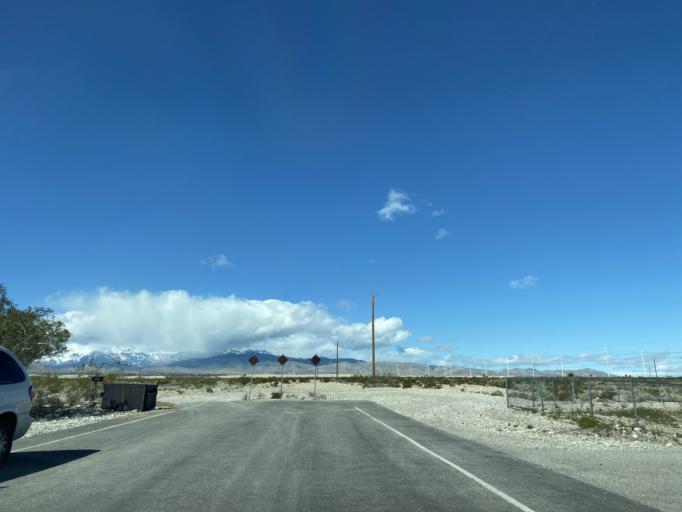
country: US
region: Nevada
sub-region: Clark County
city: North Las Vegas
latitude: 36.3321
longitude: -115.2871
